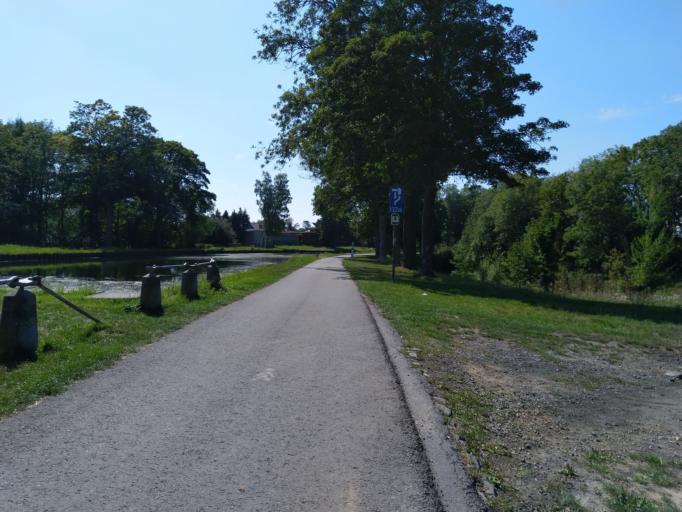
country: BE
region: Wallonia
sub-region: Province du Hainaut
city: Roeulx
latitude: 50.4741
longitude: 4.1132
